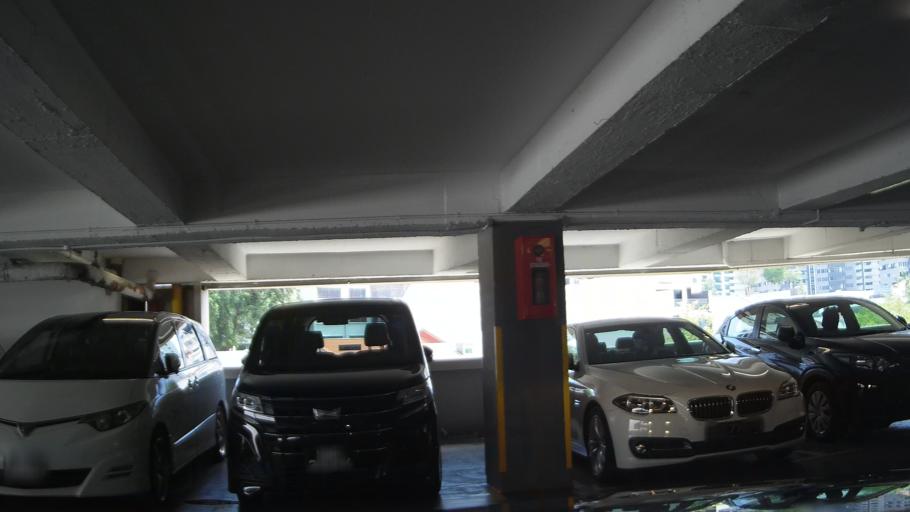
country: SG
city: Singapore
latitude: 1.2847
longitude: 103.8262
